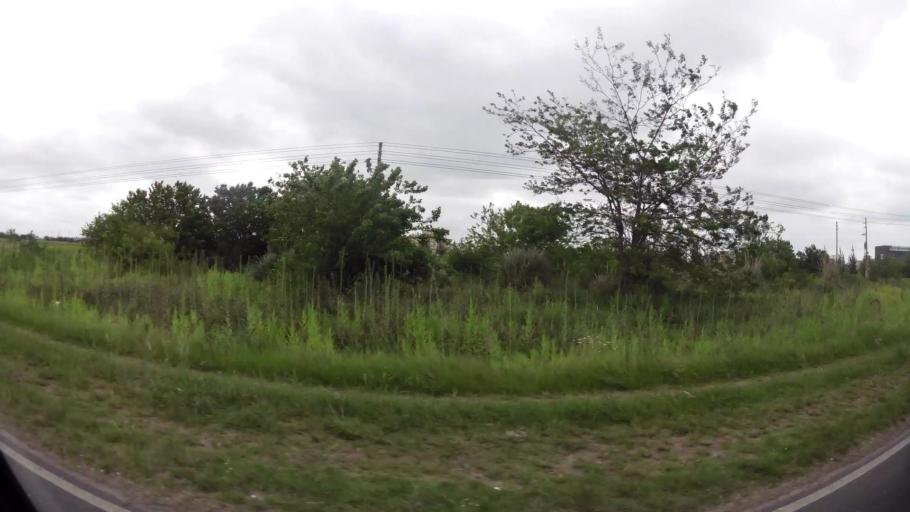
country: AR
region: Buenos Aires
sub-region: Partido de San Vicente
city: San Vicente
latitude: -34.9612
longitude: -58.4654
